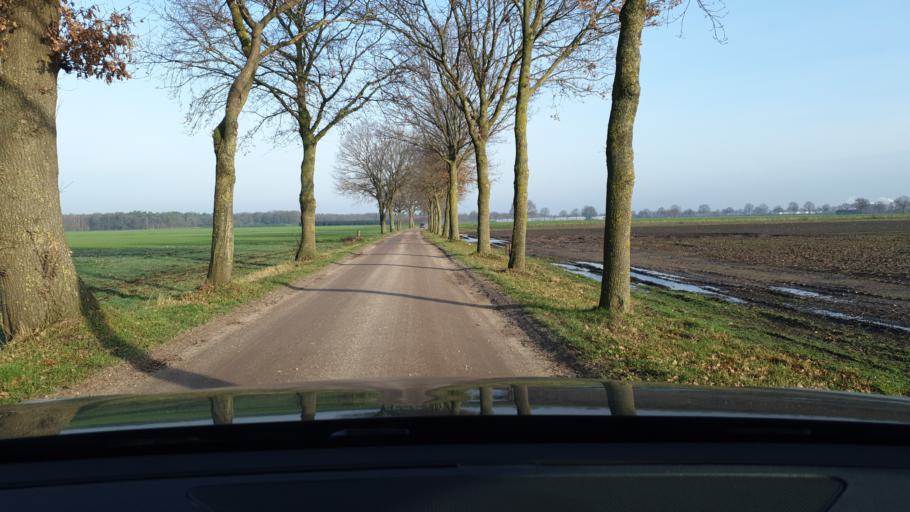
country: NL
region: Limburg
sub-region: Gemeente Peel en Maas
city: Maasbree
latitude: 51.4229
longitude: 6.0561
